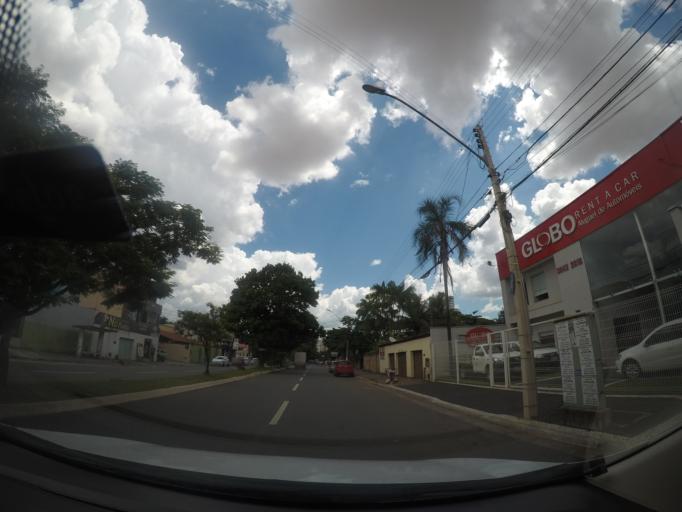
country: BR
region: Goias
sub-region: Goiania
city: Goiania
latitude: -16.7014
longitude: -49.2830
